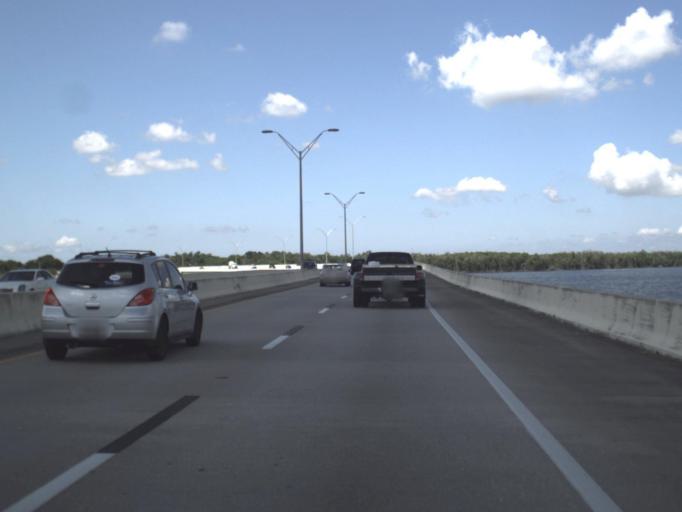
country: US
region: Florida
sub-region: Lee County
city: Whiskey Creek
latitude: 26.6060
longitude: -81.9078
